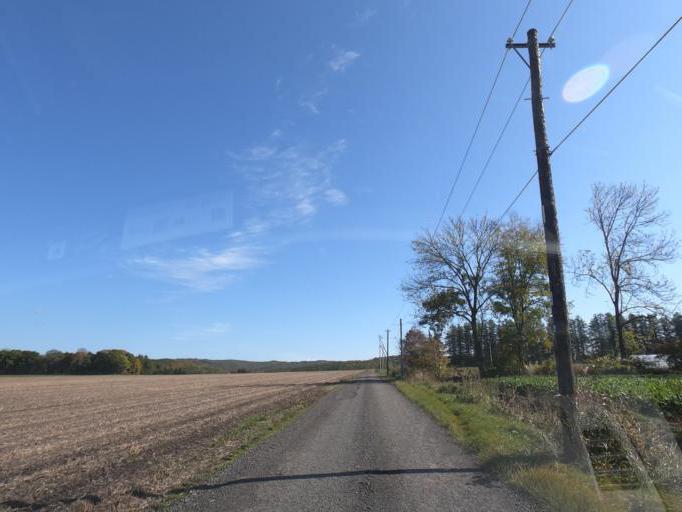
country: JP
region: Hokkaido
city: Otofuke
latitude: 43.0119
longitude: 143.2660
